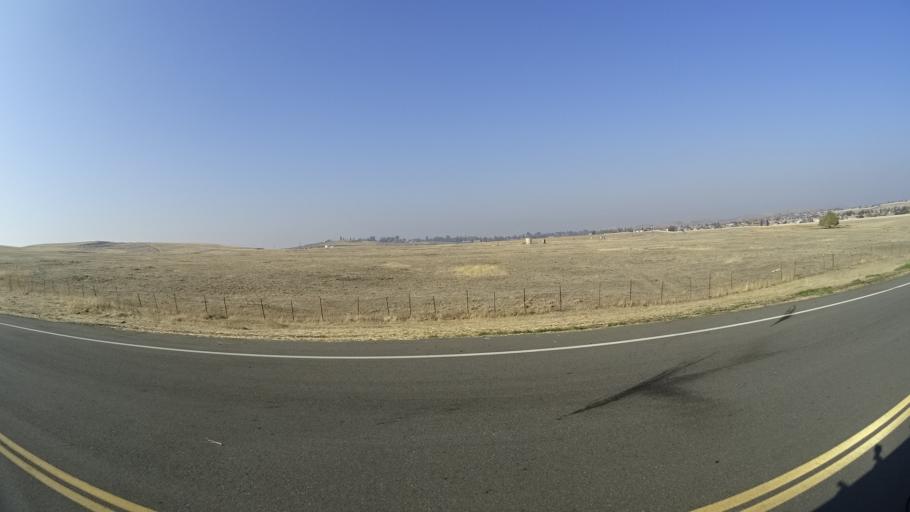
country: US
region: California
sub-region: Kern County
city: Lamont
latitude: 35.4016
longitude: -118.8454
